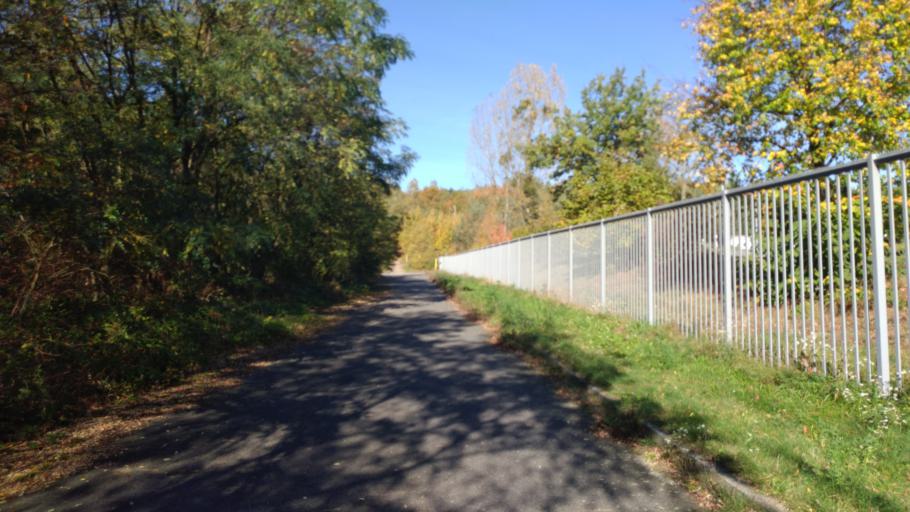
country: DE
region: Saxony
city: Albertstadt
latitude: 51.1012
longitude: 13.7291
